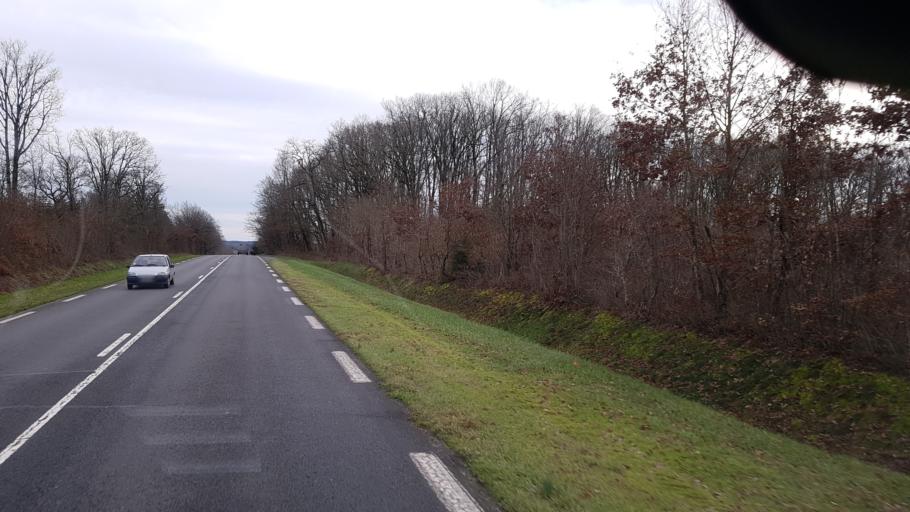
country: FR
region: Centre
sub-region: Departement du Loir-et-Cher
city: Lamotte-Beuvron
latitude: 47.6196
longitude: 2.0139
